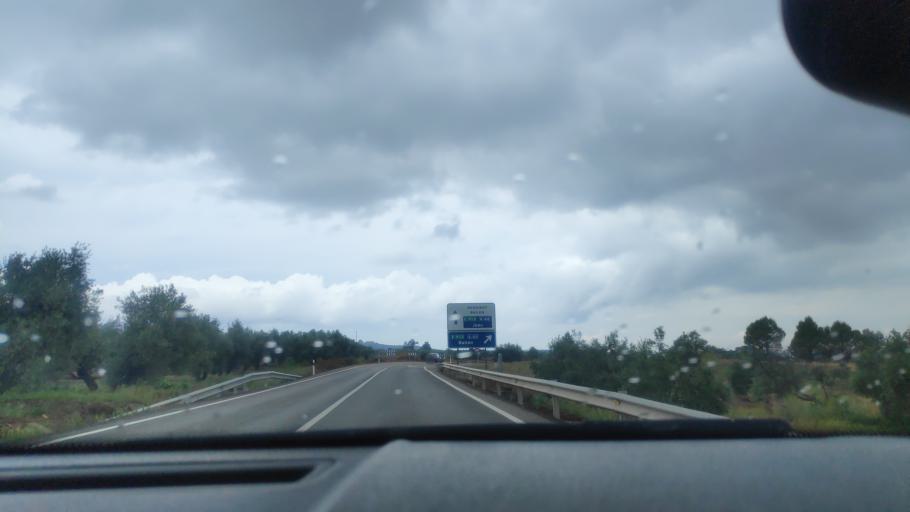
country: ES
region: Andalusia
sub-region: Provincia de Jaen
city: Jabalquinto
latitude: 38.0242
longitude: -3.7759
